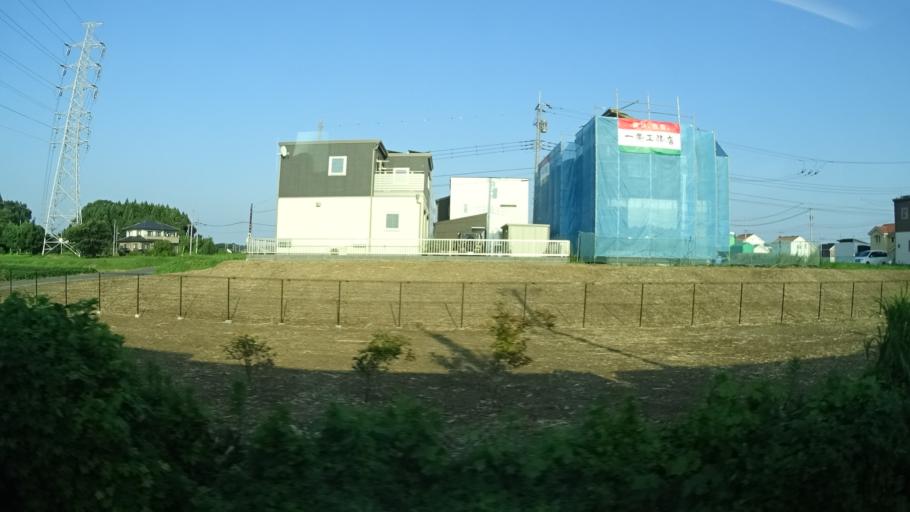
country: JP
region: Ibaraki
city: Funaishikawa
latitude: 36.4531
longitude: 140.5519
